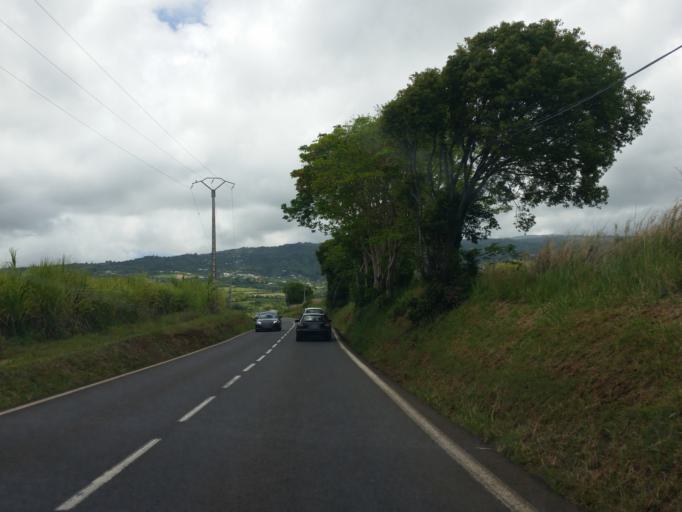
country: RE
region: Reunion
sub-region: Reunion
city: Sainte-Marie
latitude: -20.9232
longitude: 55.5375
